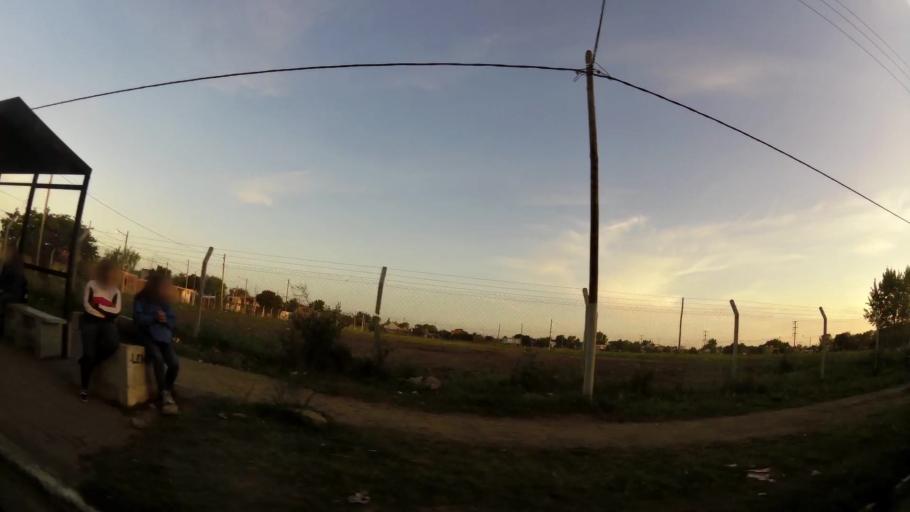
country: AR
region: Buenos Aires
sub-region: Partido de Quilmes
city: Quilmes
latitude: -34.7821
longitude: -58.2301
